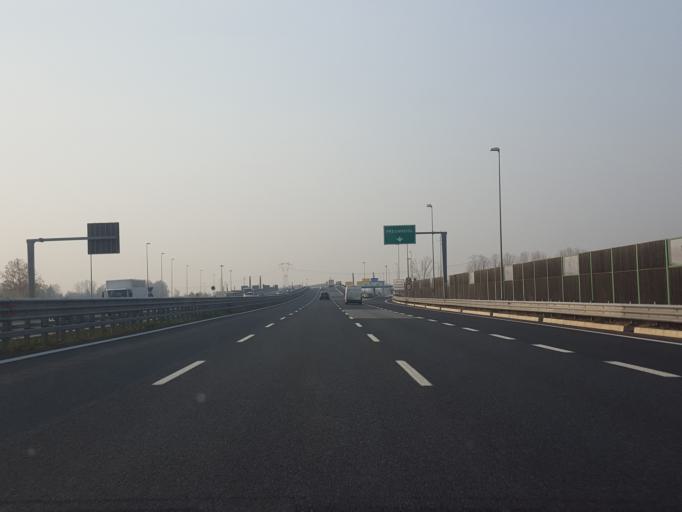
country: IT
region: Veneto
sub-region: Provincia di Treviso
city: Conscio
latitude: 45.5910
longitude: 12.2774
